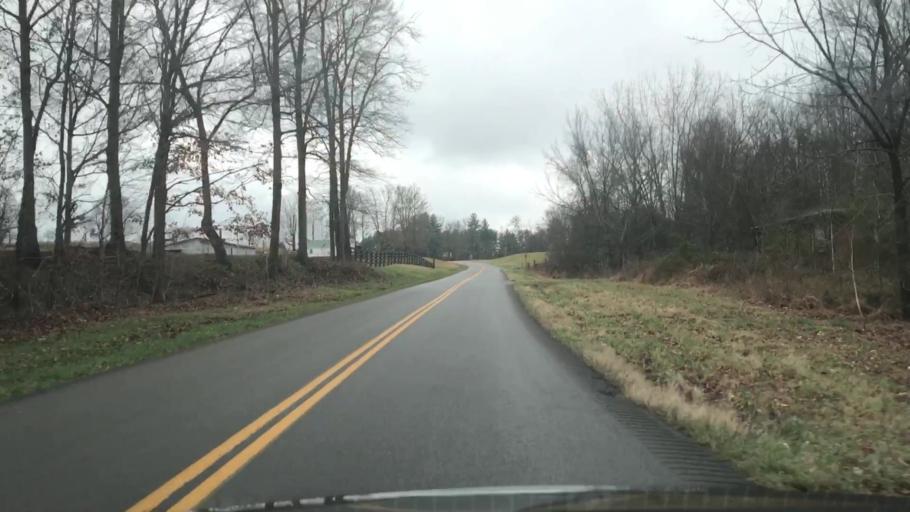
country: US
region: Kentucky
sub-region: Monroe County
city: Tompkinsville
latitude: 36.7254
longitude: -85.7097
